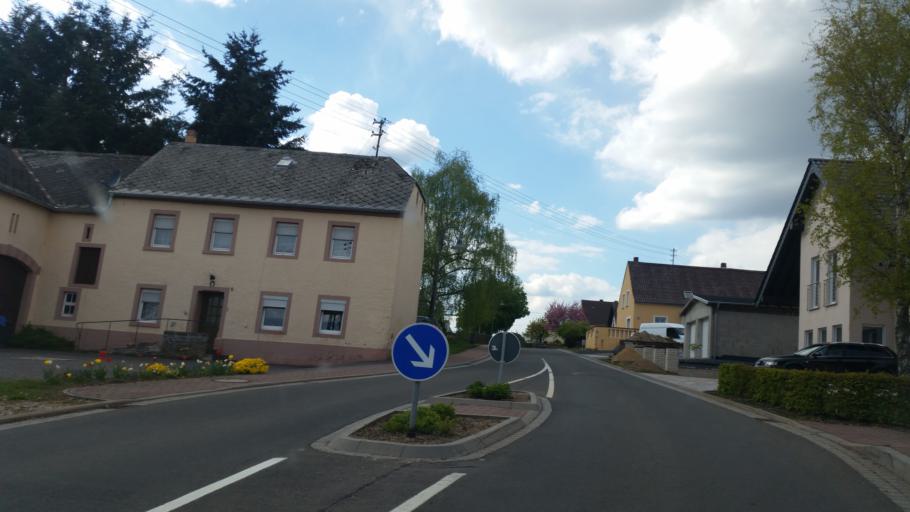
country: DE
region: Rheinland-Pfalz
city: Echtershausen
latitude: 50.0017
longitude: 6.4273
